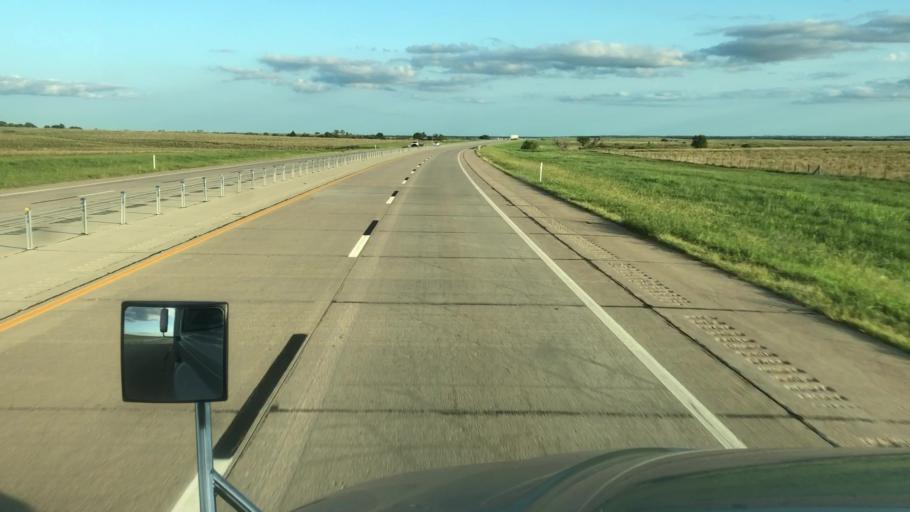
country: US
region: Oklahoma
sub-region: Pawnee County
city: Pawnee
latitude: 36.3681
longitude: -97.0360
